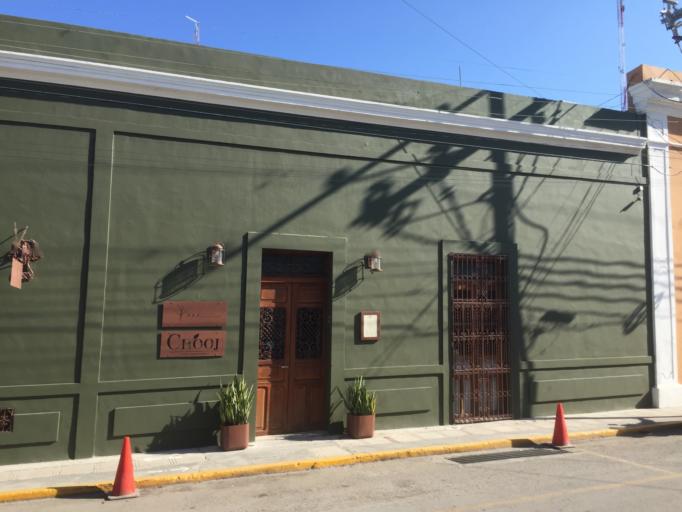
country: MX
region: Yucatan
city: Merida
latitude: 20.9691
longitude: -89.6181
